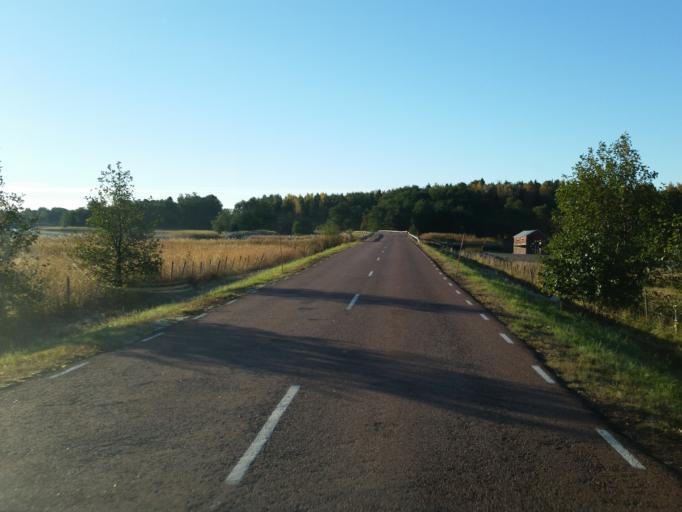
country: AX
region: Alands skaergard
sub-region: Vardoe
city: Vardoe
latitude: 60.2387
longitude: 20.3737
